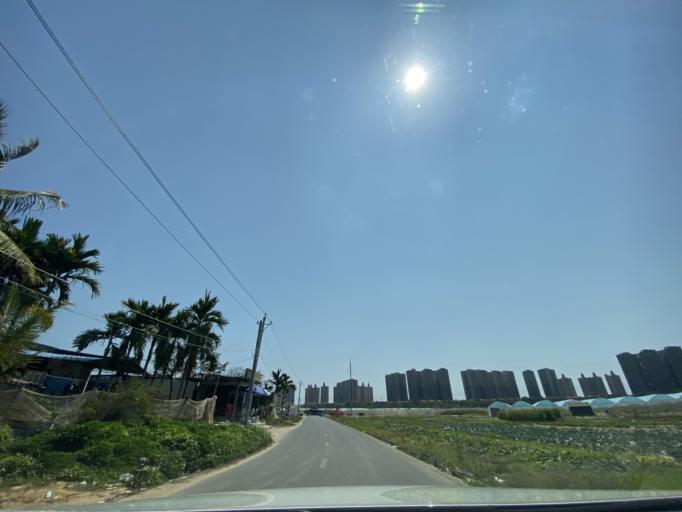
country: CN
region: Hainan
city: Yingzhou
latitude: 18.4207
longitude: 109.8779
